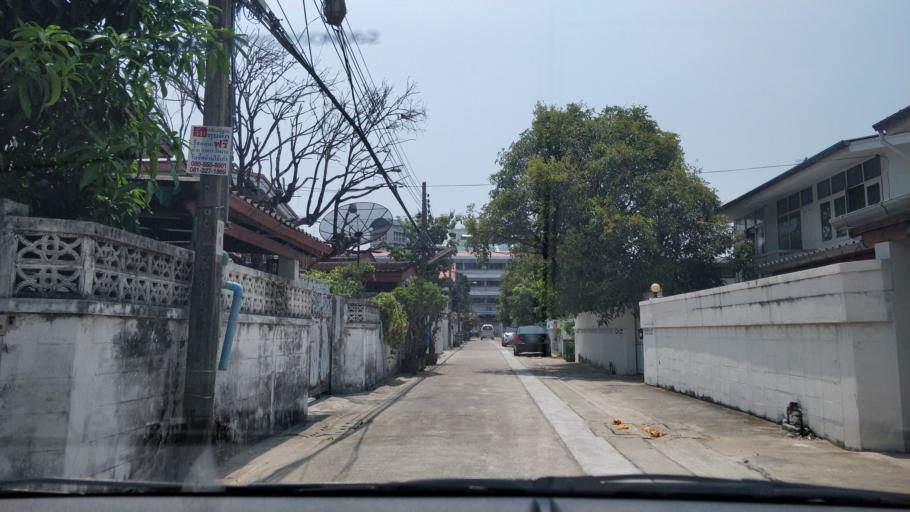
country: TH
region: Bangkok
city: Watthana
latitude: 13.7292
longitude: 100.6022
